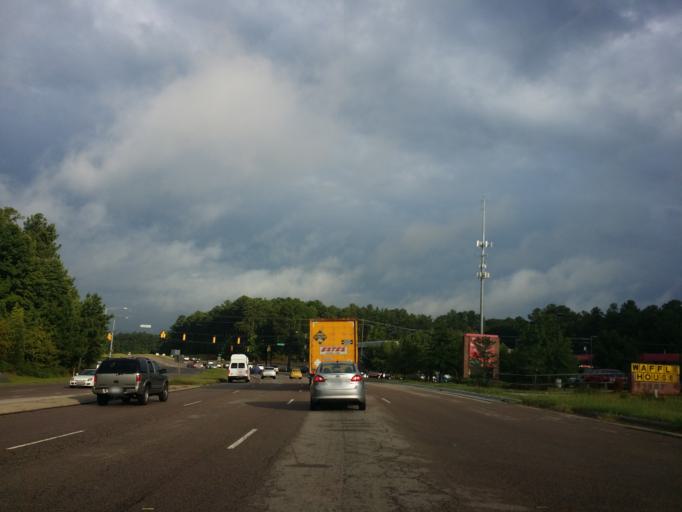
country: US
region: North Carolina
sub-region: Durham County
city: Durham
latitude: 35.9237
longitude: -78.8451
